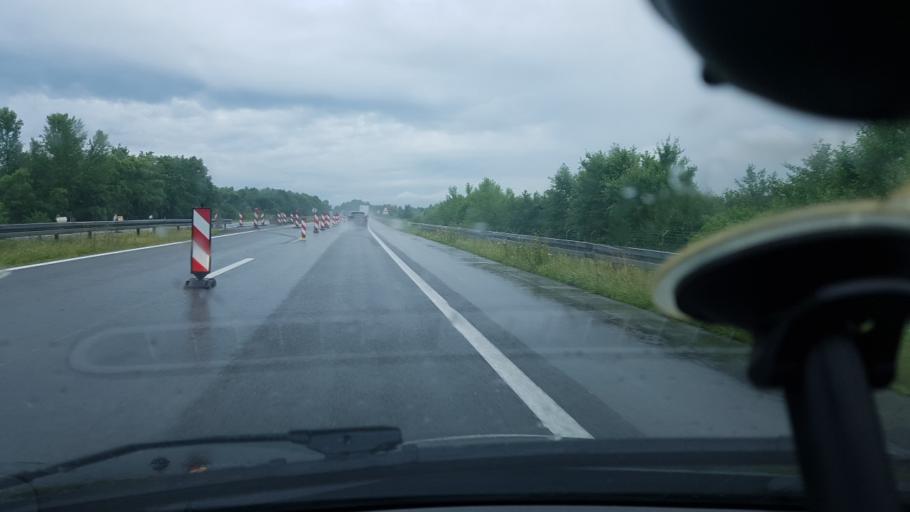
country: HR
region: Zagrebacka
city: Pojatno
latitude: 45.9207
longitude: 15.8253
